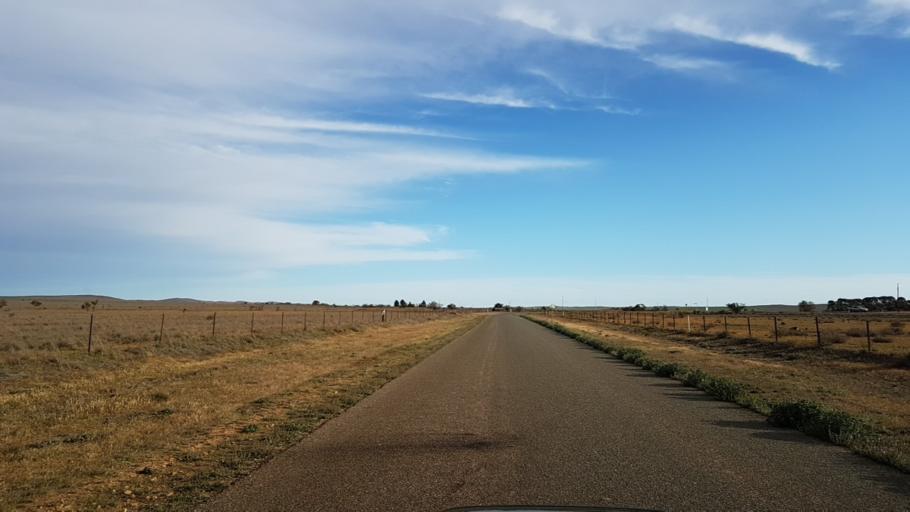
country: AU
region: South Australia
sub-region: Peterborough
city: Peterborough
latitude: -32.9881
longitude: 138.8497
